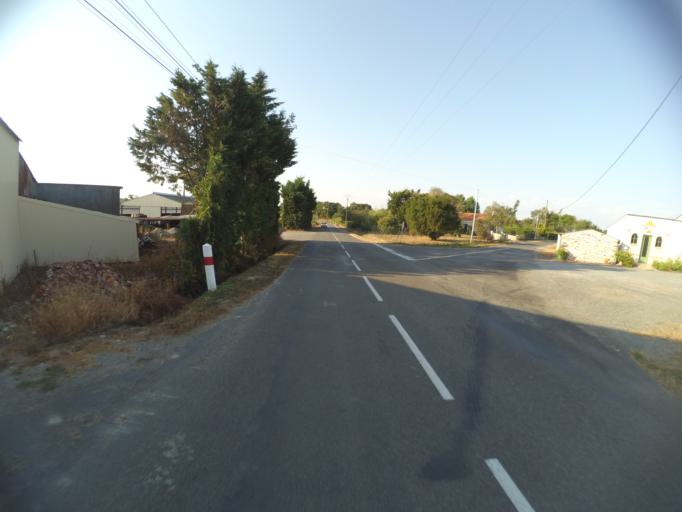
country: FR
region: Pays de la Loire
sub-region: Departement de la Loire-Atlantique
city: Aigrefeuille-sur-Maine
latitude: 47.0576
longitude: -1.4127
